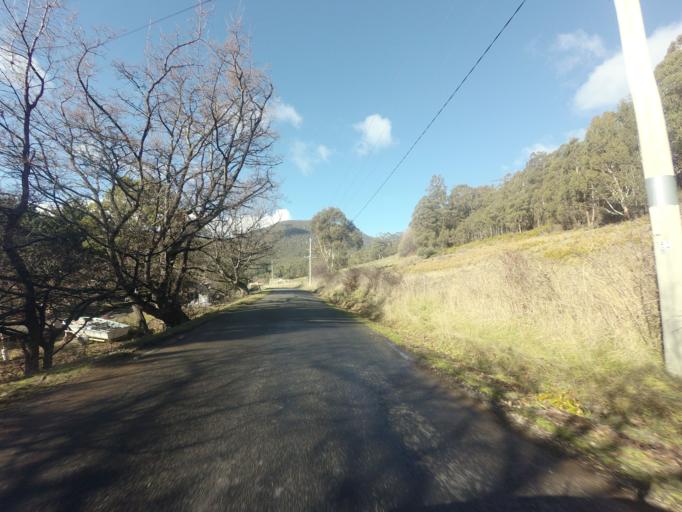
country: AU
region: Tasmania
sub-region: Glenorchy
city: Berriedale
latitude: -42.8414
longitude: 147.1862
